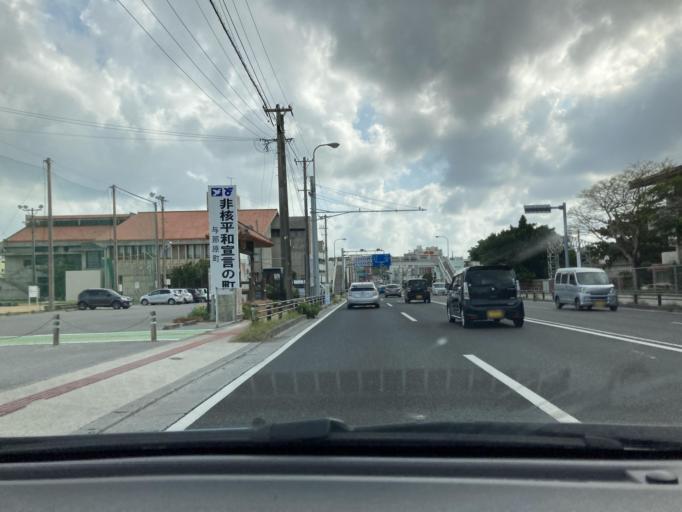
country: JP
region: Okinawa
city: Ginowan
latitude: 26.2045
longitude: 127.7556
